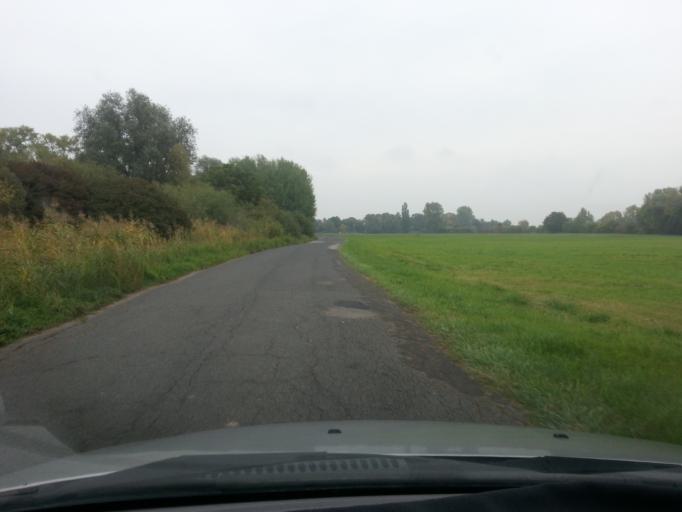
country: DE
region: Rheinland-Pfalz
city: Lachen-Speyerdorf
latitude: 49.3249
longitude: 8.2120
